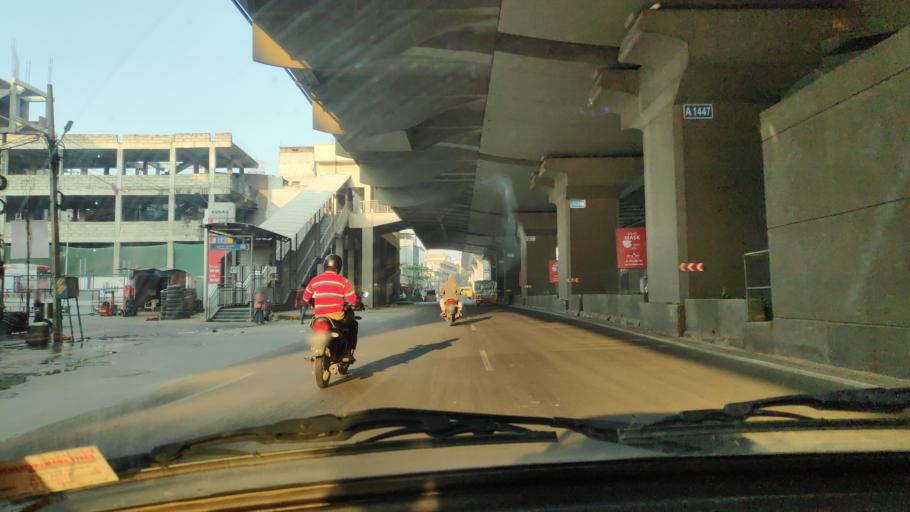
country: IN
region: Telangana
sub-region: Rangareddi
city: Gaddi Annaram
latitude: 17.3734
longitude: 78.5033
